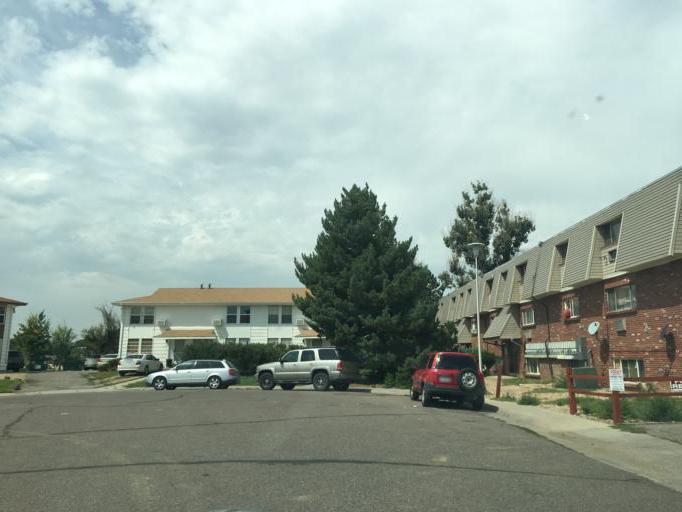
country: US
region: Colorado
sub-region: Adams County
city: Aurora
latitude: 39.7379
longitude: -104.7967
